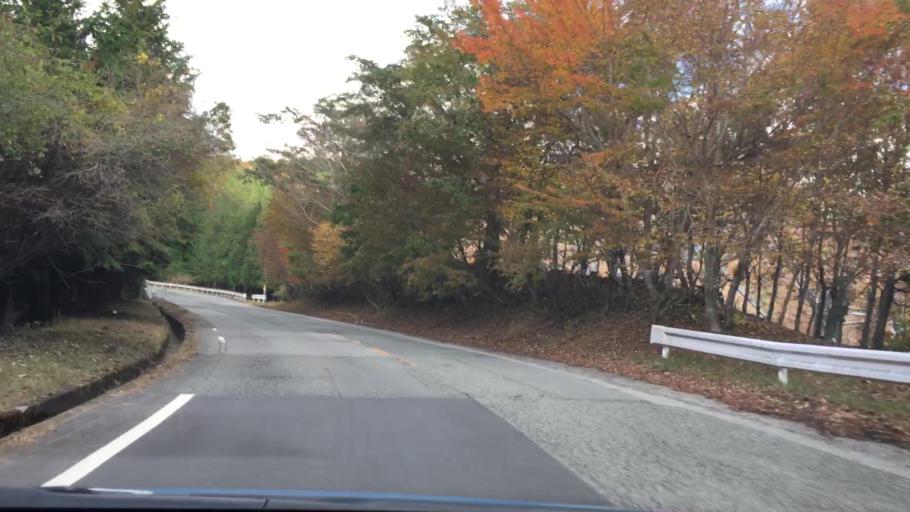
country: JP
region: Shizuoka
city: Gotemba
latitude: 35.3942
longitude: 138.9431
